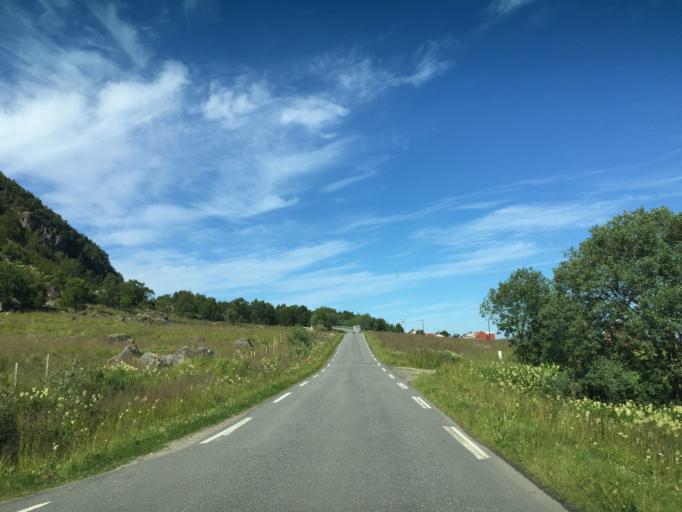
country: NO
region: Nordland
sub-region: Vagan
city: Svolvaer
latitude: 68.3989
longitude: 14.5301
